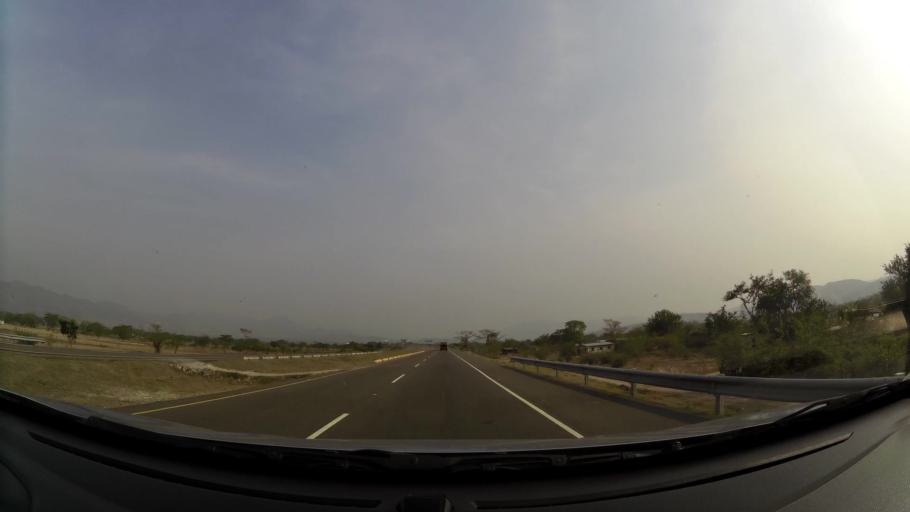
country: HN
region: Comayagua
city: Comayagua
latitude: 14.4540
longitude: -87.6648
